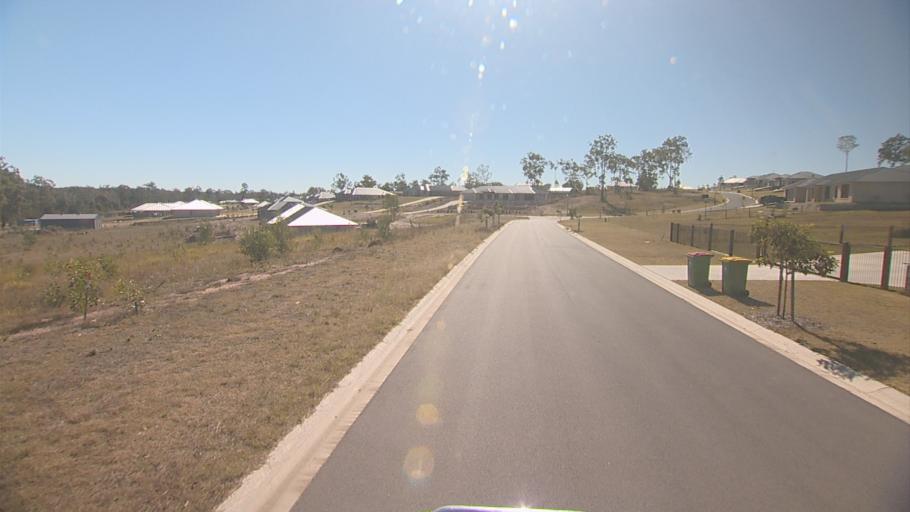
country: AU
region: Queensland
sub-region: Logan
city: North Maclean
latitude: -27.7514
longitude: 152.9439
